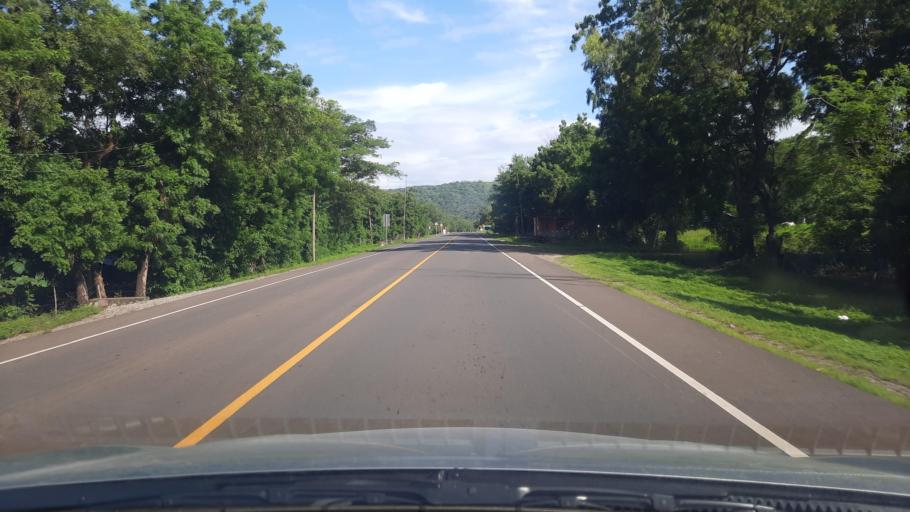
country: NI
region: Leon
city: Telica
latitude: 12.7095
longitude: -86.8727
